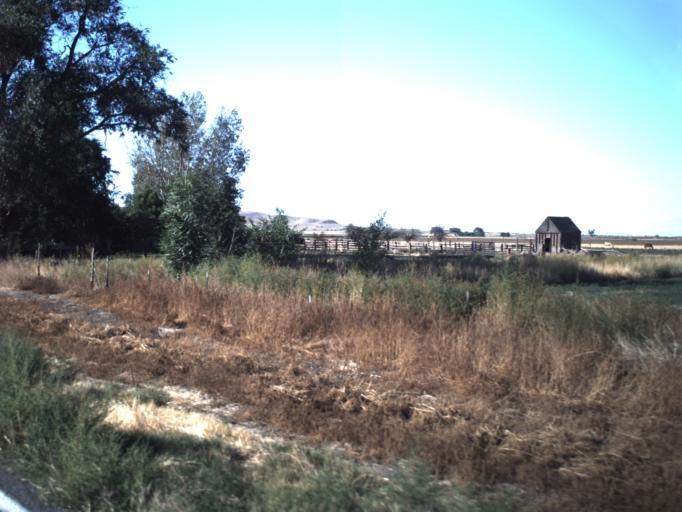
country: US
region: Utah
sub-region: Millard County
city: Delta
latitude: 39.4865
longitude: -112.2689
